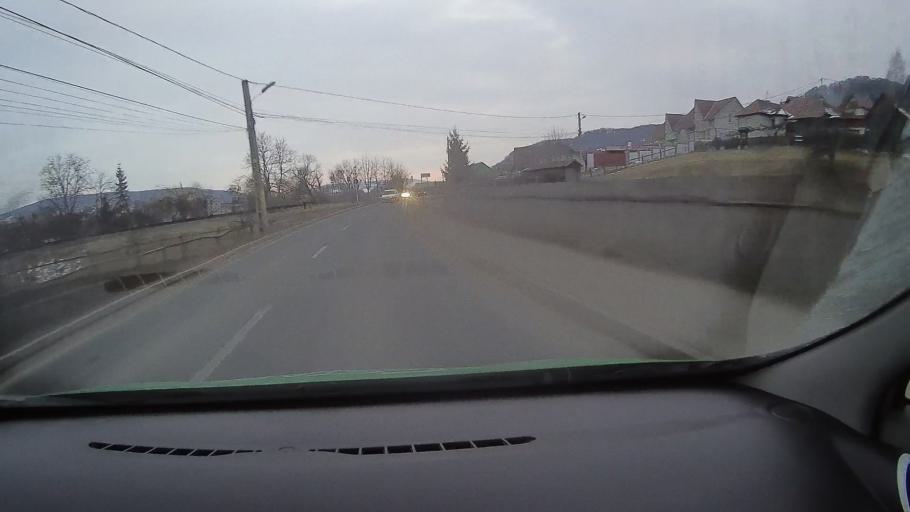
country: RO
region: Harghita
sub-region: Municipiul Odorheiu Secuiesc
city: Odorheiu Secuiesc
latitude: 46.3067
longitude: 25.2856
